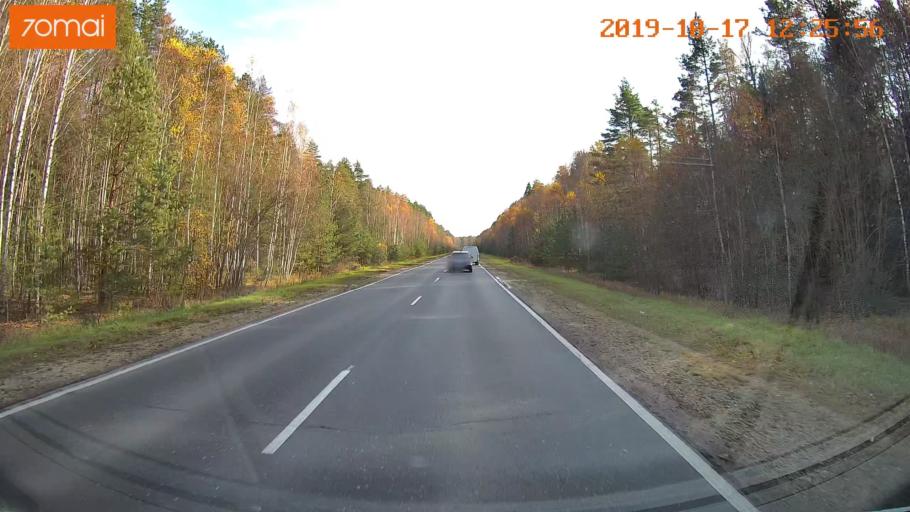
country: RU
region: Rjazan
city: Syntul
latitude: 55.0236
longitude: 41.2455
